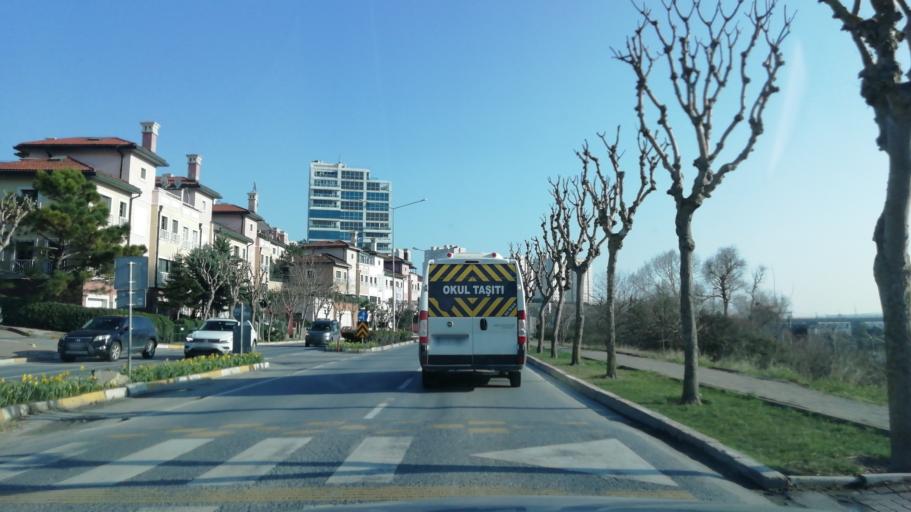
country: TR
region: Istanbul
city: Esenyurt
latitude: 41.0660
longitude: 28.6979
